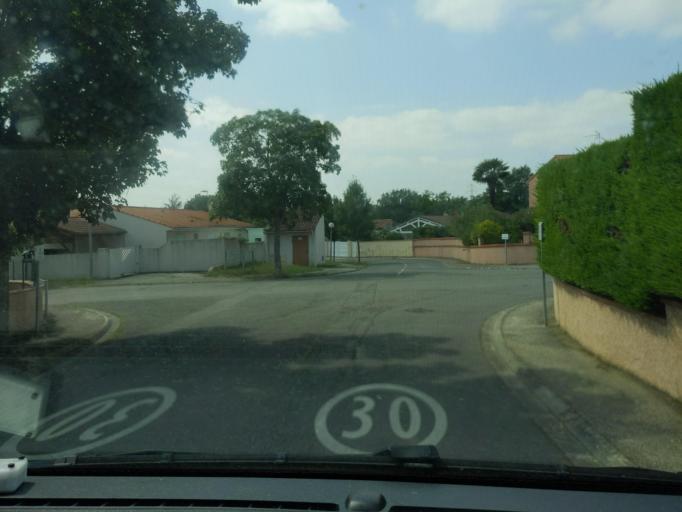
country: FR
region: Midi-Pyrenees
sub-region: Departement de la Haute-Garonne
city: Balma
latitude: 43.6127
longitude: 1.5121
